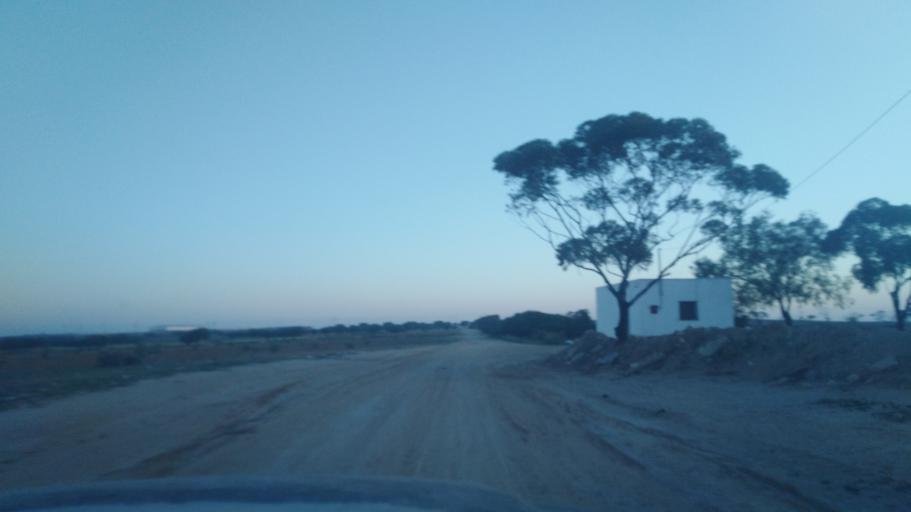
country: TN
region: Safaqis
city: Sfax
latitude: 34.7293
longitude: 10.4460
